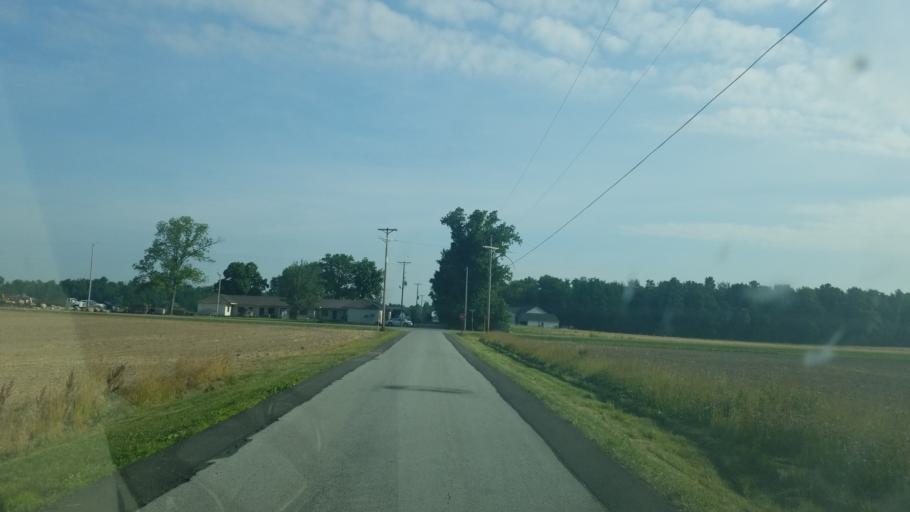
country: US
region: Ohio
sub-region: Hancock County
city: Arlington
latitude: 40.8332
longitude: -83.6705
